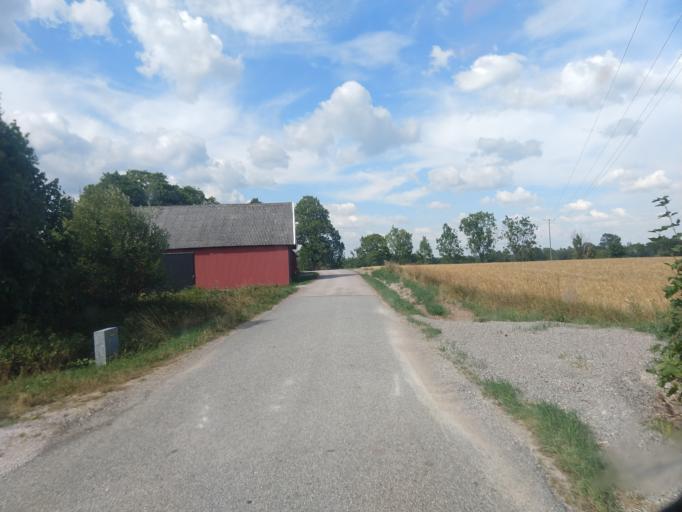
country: SE
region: Blekinge
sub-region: Karlskrona Kommun
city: Nattraby
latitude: 56.2507
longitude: 15.5266
